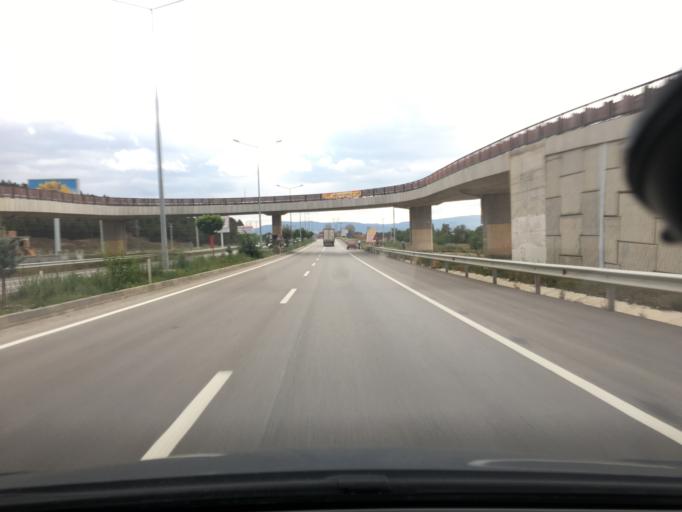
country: TR
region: Afyonkarahisar
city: Sincanli
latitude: 38.7908
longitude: 30.3824
